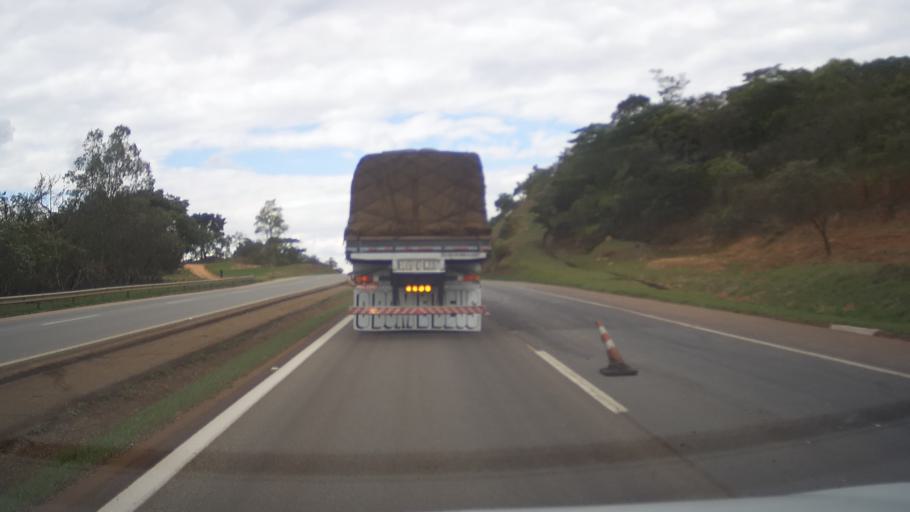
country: BR
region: Minas Gerais
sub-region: Itauna
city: Itauna
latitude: -20.3177
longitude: -44.4537
